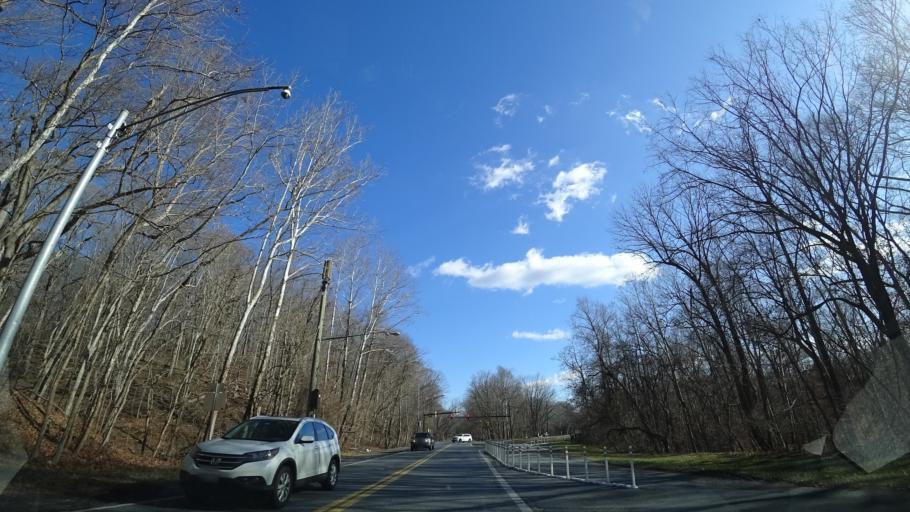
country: US
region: Maryland
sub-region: Montgomery County
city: Potomac
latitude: 38.9793
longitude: -77.2080
